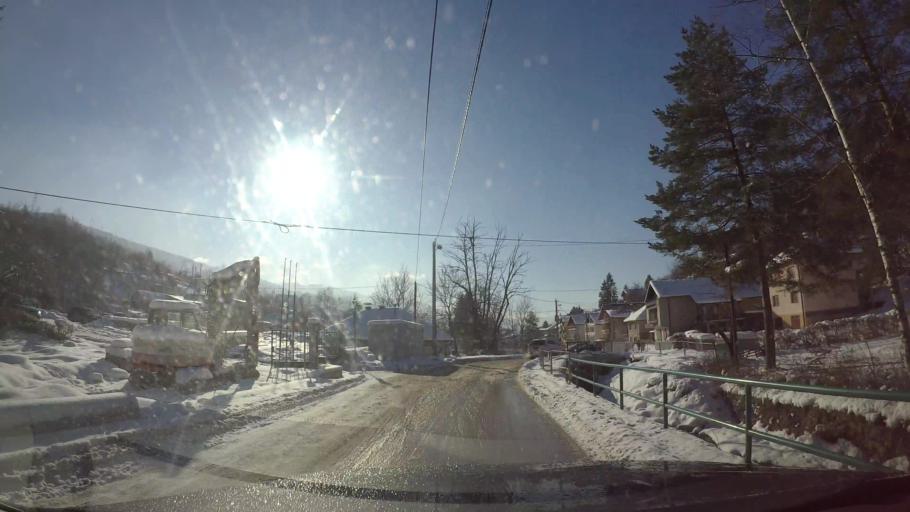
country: BA
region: Federation of Bosnia and Herzegovina
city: Kobilja Glava
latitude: 43.8871
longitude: 18.4160
